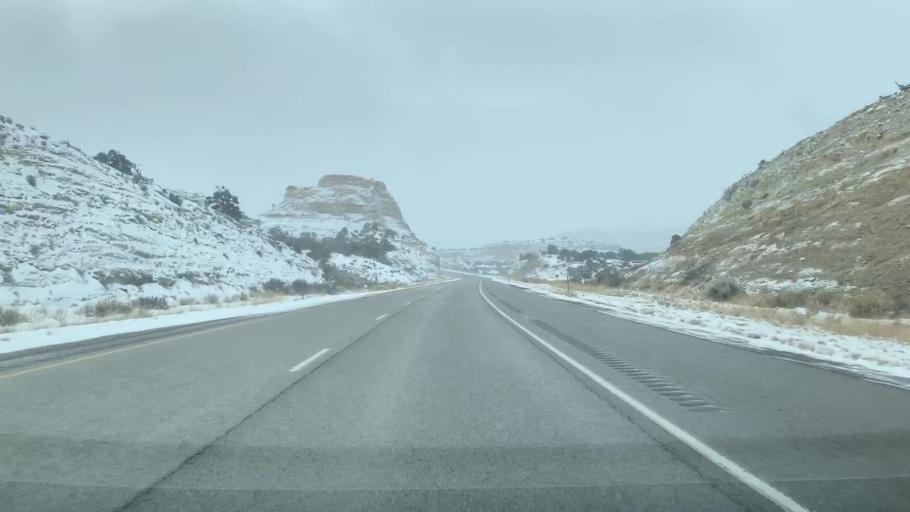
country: US
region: Utah
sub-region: Emery County
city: Ferron
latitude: 38.8557
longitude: -110.8736
